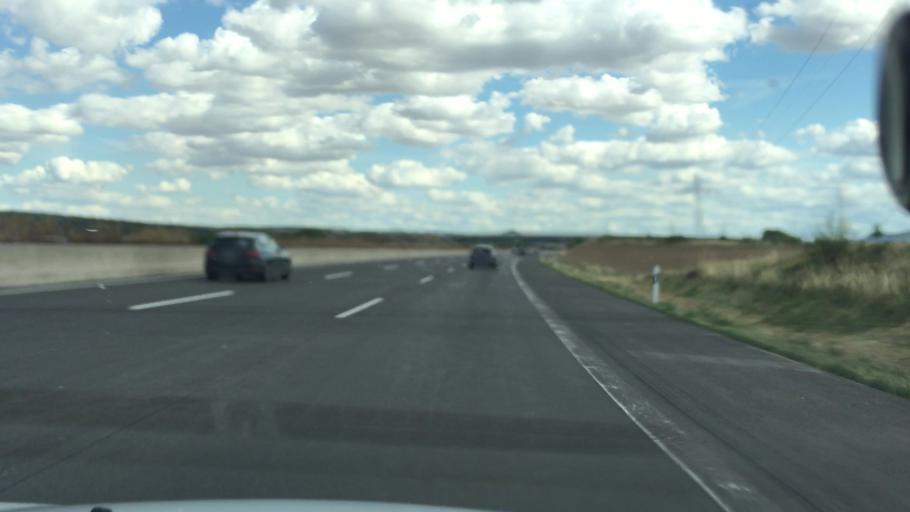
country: DE
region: Thuringia
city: Bischofroda
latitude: 51.0156
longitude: 10.3746
